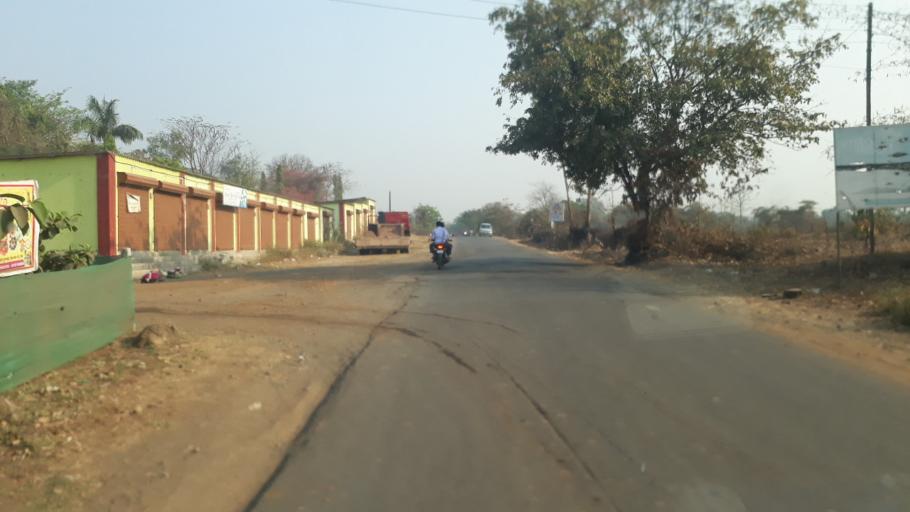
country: IN
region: Maharashtra
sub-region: Raigarh
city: Neral
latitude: 19.0446
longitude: 73.3318
